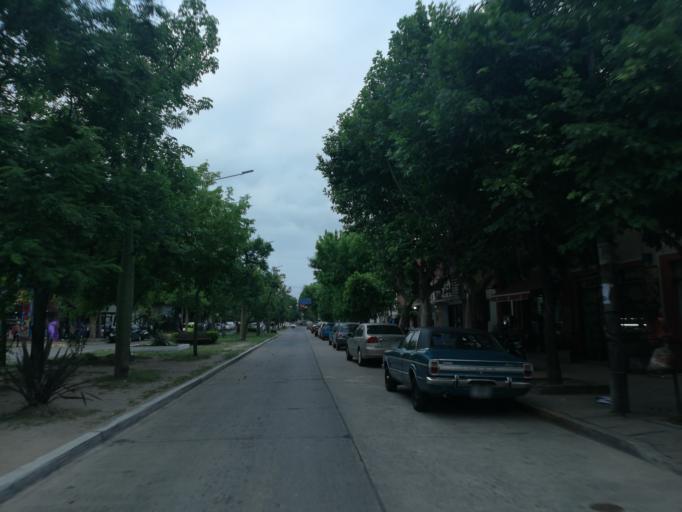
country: AR
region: Buenos Aires
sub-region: Partido de La Plata
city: La Plata
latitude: -34.8517
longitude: -58.0770
